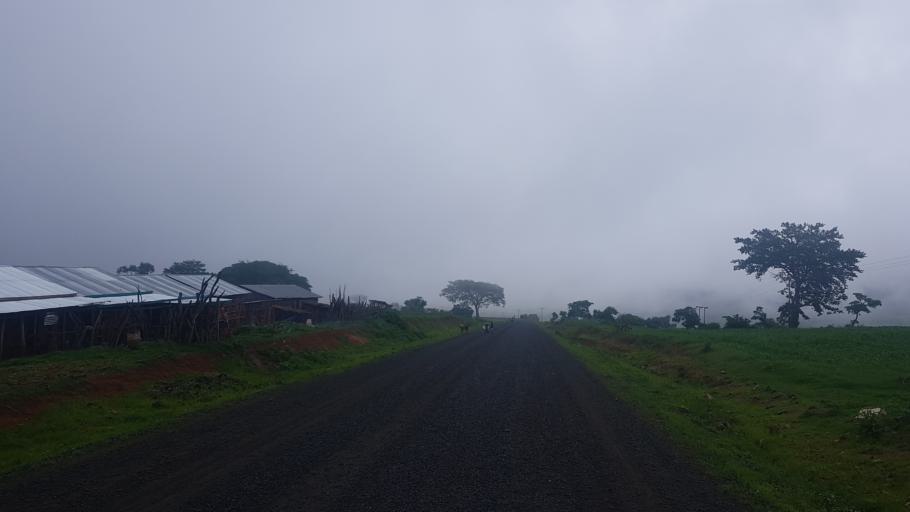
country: ET
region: Amhara
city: Bure
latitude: 10.1943
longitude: 36.9718
